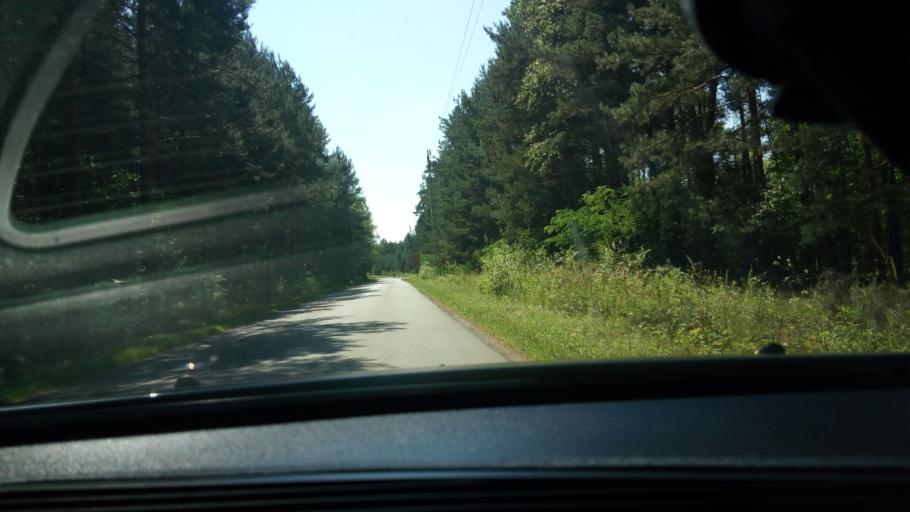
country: PL
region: Lesser Poland Voivodeship
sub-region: Powiat chrzanowski
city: Zarki
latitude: 50.1079
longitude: 19.3675
